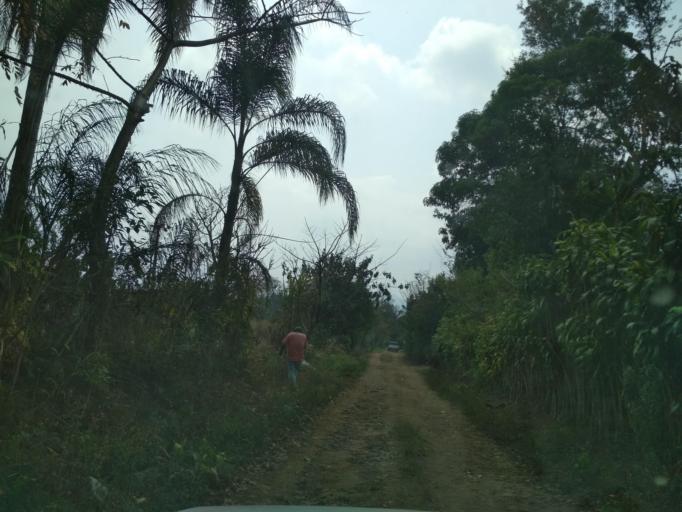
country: MX
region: Veracruz
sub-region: Cordoba
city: Fredepo
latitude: 18.8559
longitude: -96.9793
